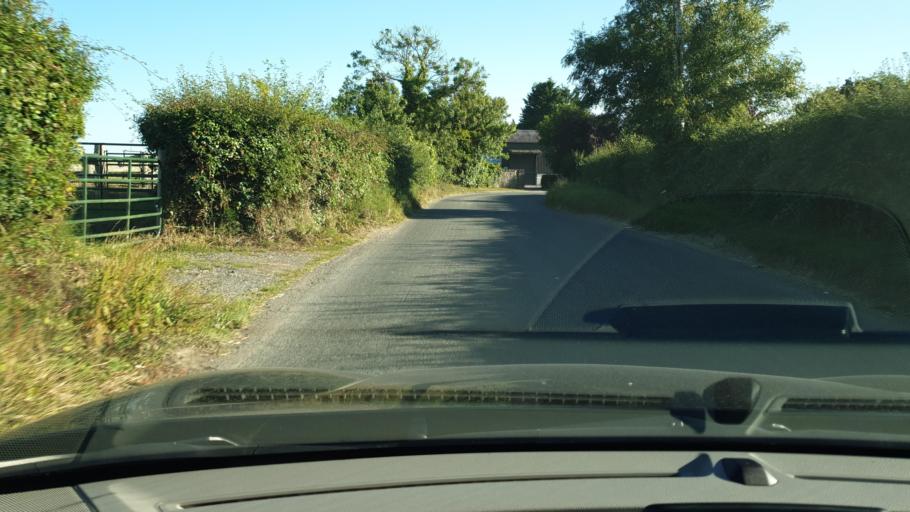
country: IE
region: Leinster
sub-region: An Mhi
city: Ashbourne
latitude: 53.4614
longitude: -6.3811
